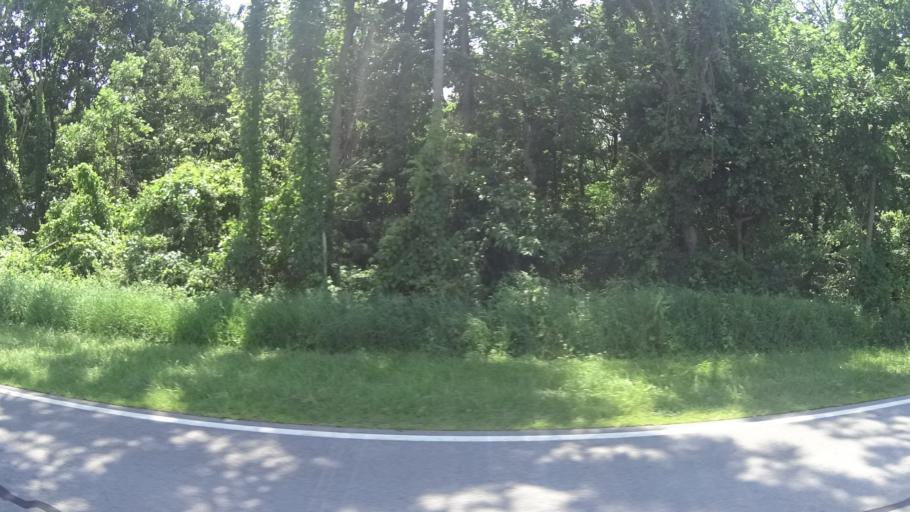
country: US
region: Ohio
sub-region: Erie County
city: Huron
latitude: 41.3684
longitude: -82.5419
